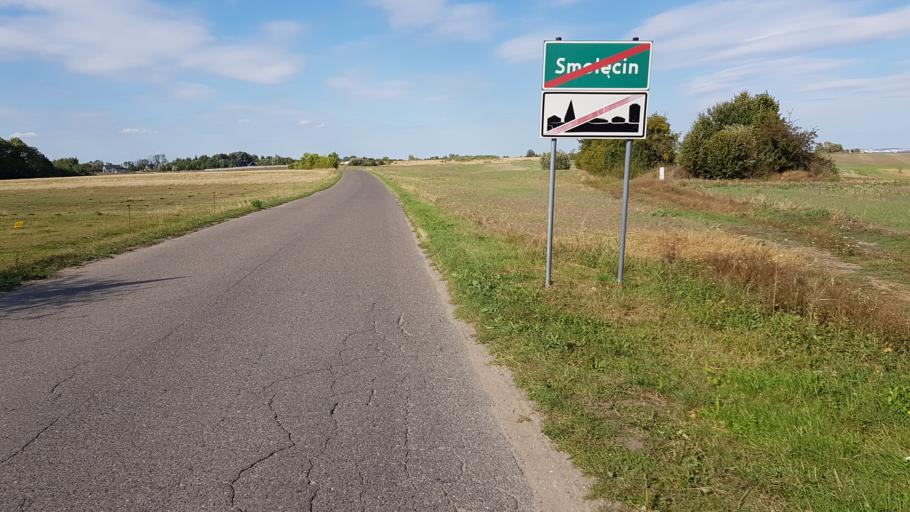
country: PL
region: West Pomeranian Voivodeship
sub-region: Powiat policki
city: Kolbaskowo
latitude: 53.3601
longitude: 14.4398
